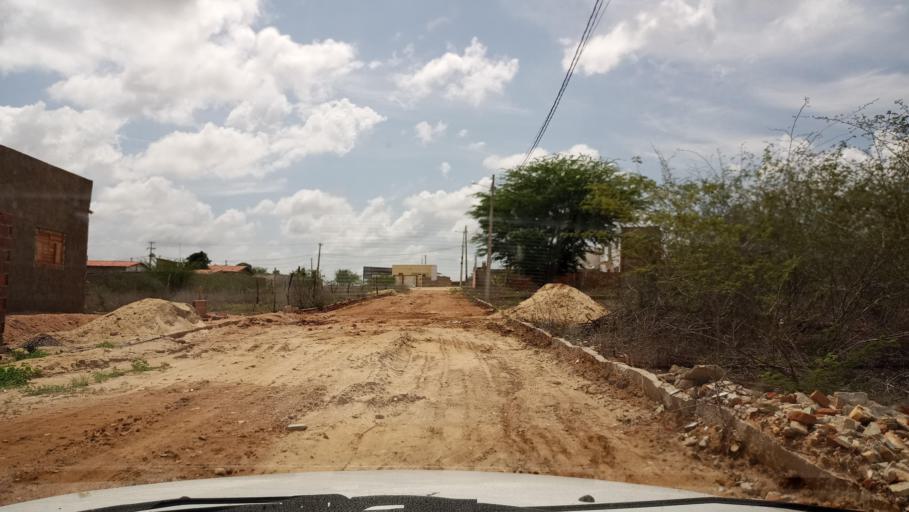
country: BR
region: Rio Grande do Norte
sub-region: Tangara
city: Tangara
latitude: -6.1127
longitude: -35.7180
